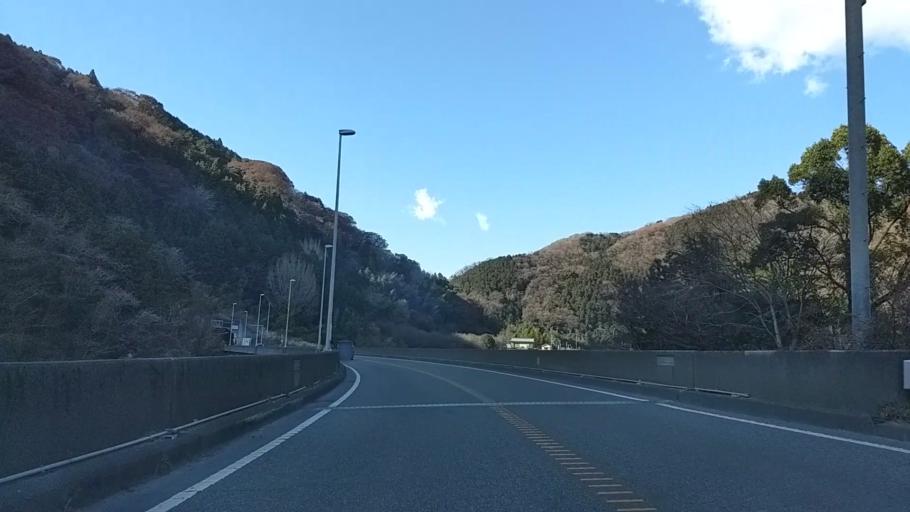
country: JP
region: Shizuoka
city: Gotemba
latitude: 35.3601
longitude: 139.0579
